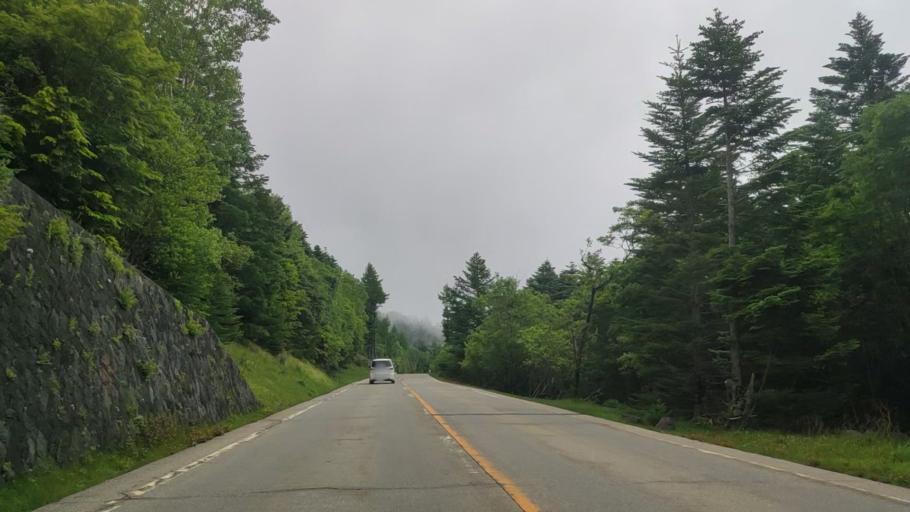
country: JP
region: Yamanashi
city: Fujikawaguchiko
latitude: 35.3865
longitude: 138.6905
